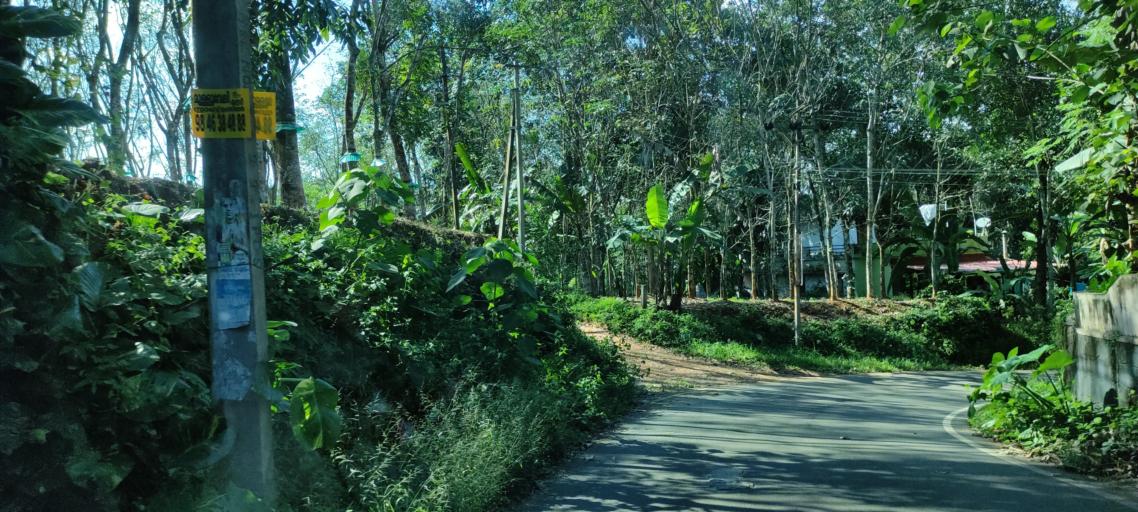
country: IN
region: Kerala
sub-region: Pattanamtitta
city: Adur
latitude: 9.2021
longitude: 76.7483
